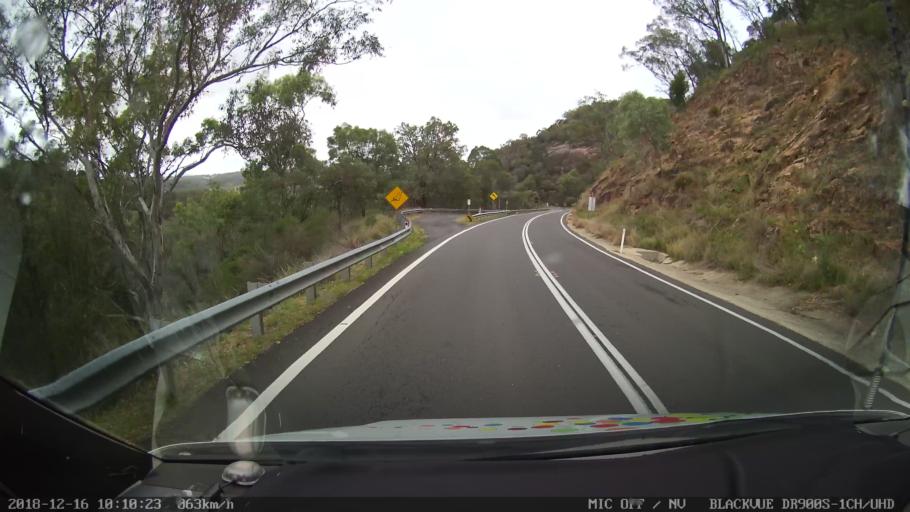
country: AU
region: New South Wales
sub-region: Glen Innes Severn
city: Glen Innes
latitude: -29.3184
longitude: 151.9238
